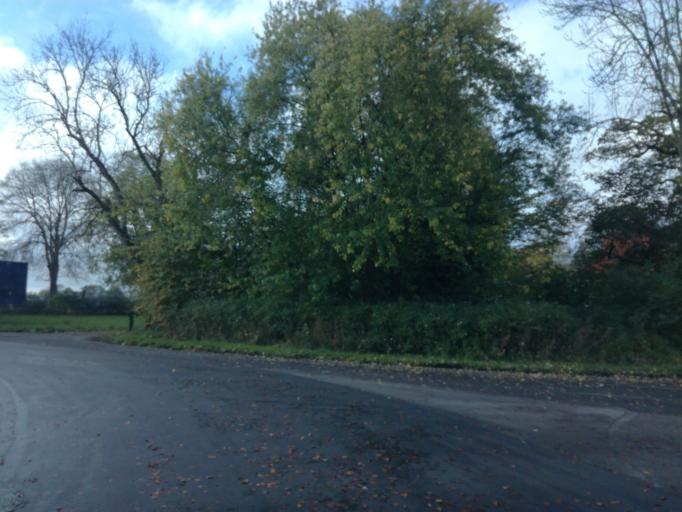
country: DK
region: South Denmark
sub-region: Vejle Kommune
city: Brejning
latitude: 55.6515
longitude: 9.6623
